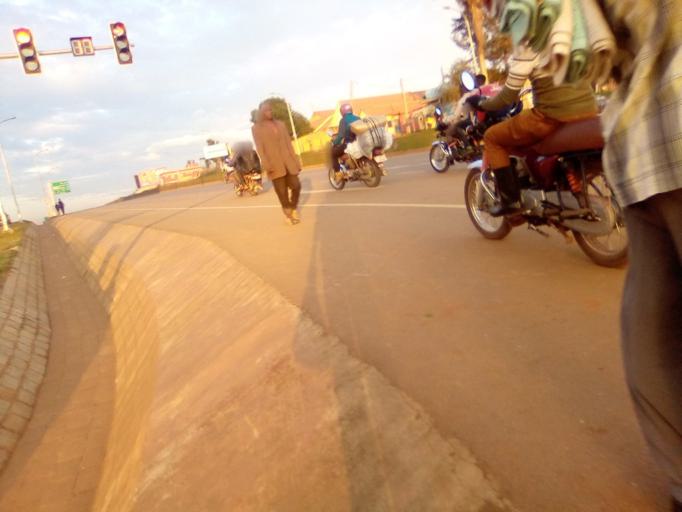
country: UG
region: Central Region
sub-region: Wakiso District
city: Entebbe
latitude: 0.0991
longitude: 32.5063
